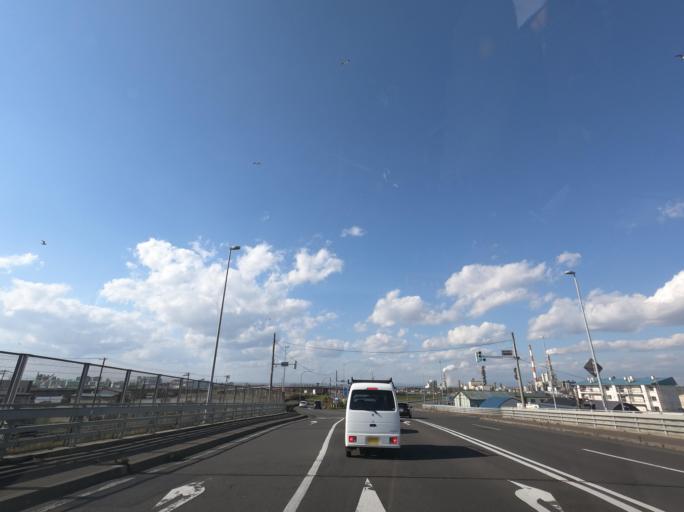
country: JP
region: Hokkaido
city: Kushiro
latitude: 42.9978
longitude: 144.3630
